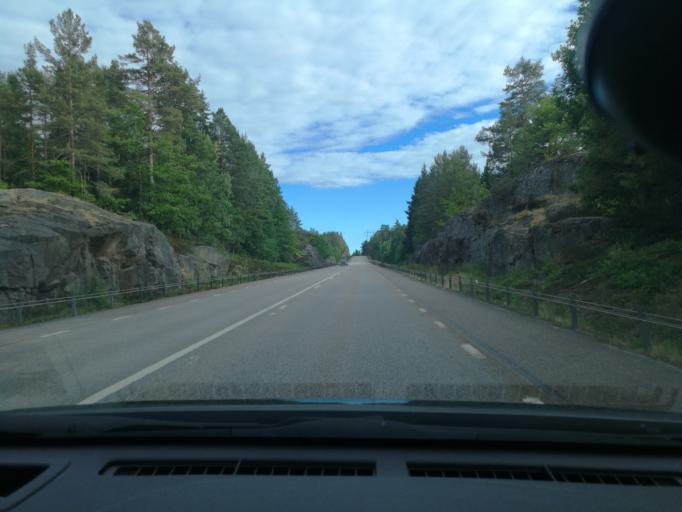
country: SE
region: Kalmar
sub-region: Vasterviks Kommun
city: Ankarsrum
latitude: 57.5417
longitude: 16.4803
